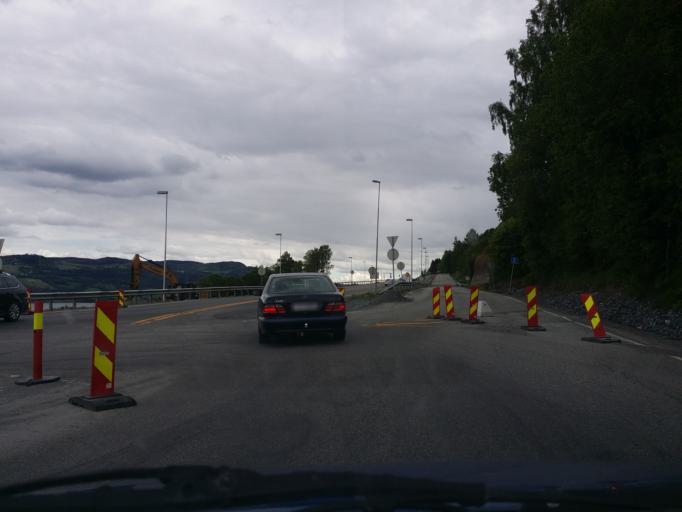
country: NO
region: Hedmark
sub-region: Ringsaker
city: Moelv
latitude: 60.9842
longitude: 10.5632
